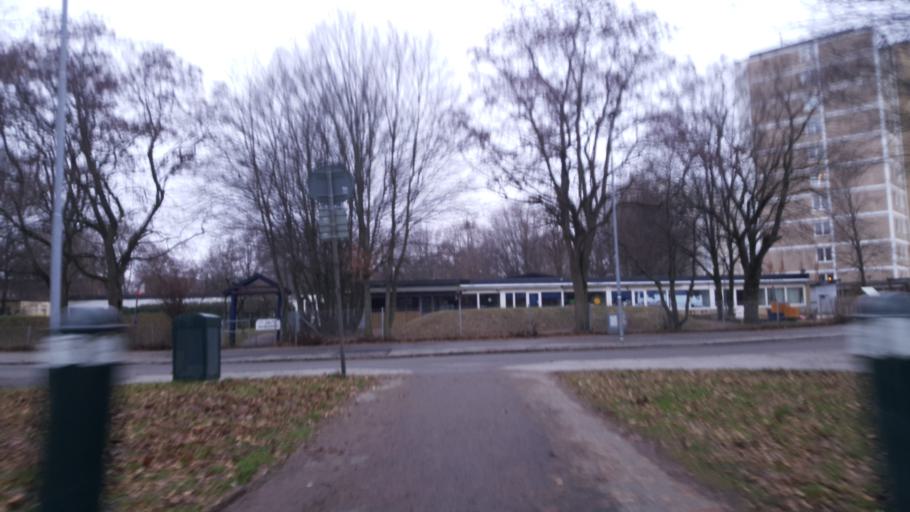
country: SE
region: Skane
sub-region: Lunds Kommun
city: Lund
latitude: 55.6929
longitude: 13.1936
